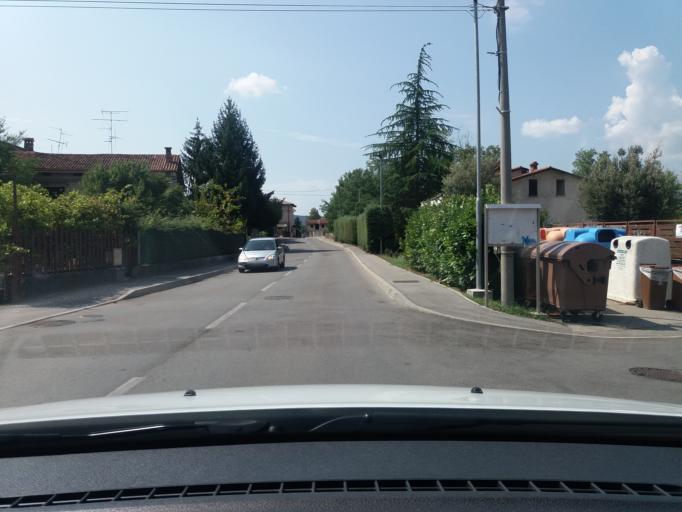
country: SI
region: Sempeter-Vrtojba
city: Vrtojba
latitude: 45.9062
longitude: 13.6290
